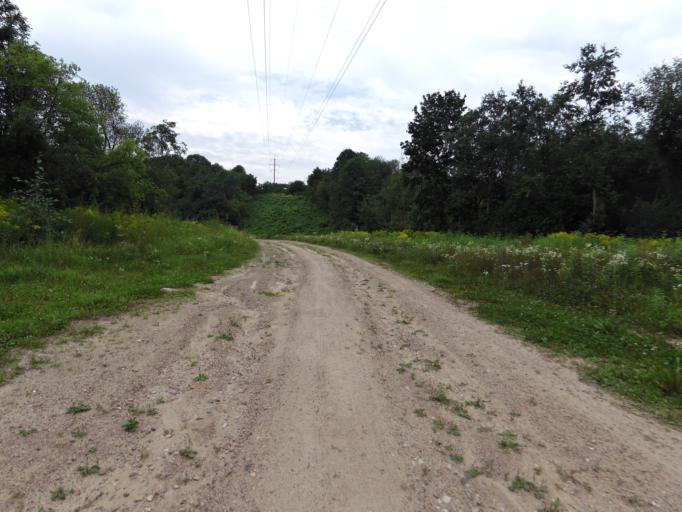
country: LT
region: Vilnius County
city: Seskine
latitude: 54.7217
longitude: 25.2791
